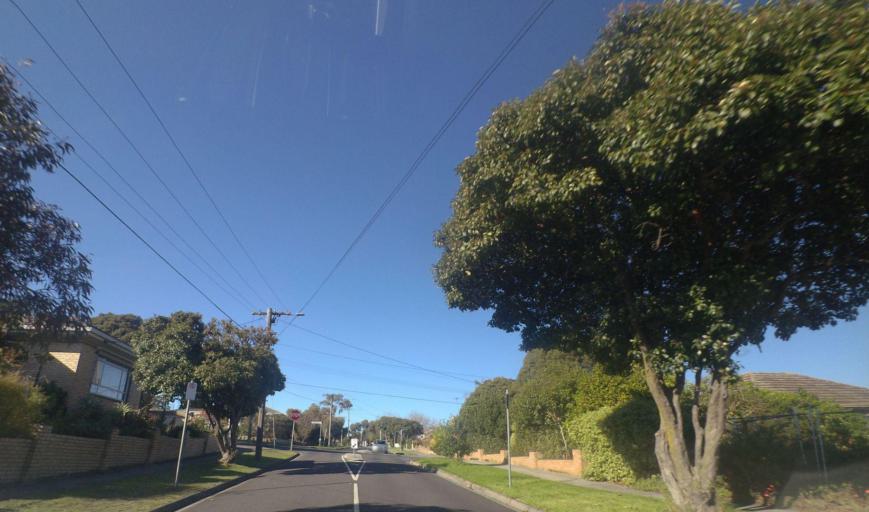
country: AU
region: Victoria
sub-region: Whitehorse
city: Box Hill North
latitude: -37.8077
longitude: 145.1356
